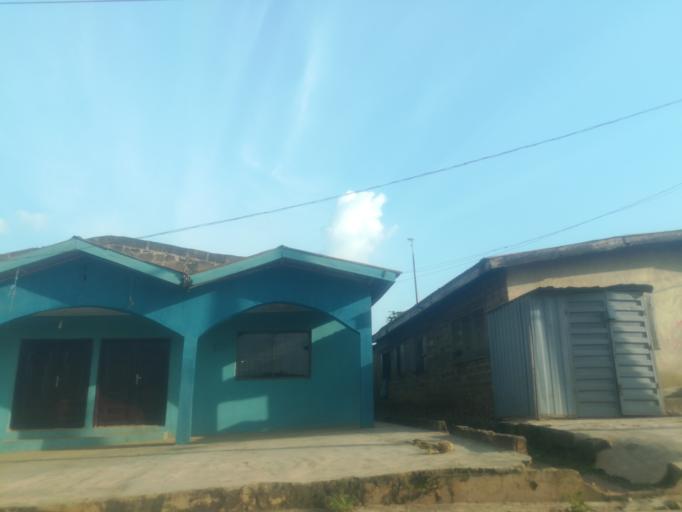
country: NG
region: Oyo
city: Ibadan
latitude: 7.3790
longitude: 3.8162
